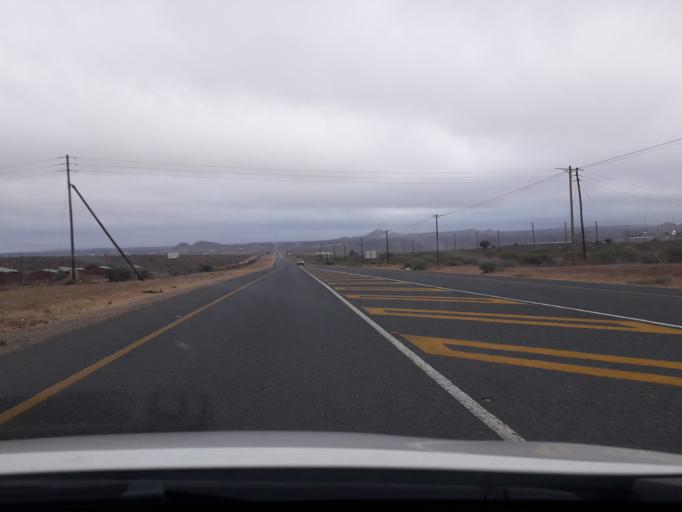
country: ZA
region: Limpopo
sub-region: Capricorn District Municipality
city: Dendron
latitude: -23.4739
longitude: 29.7306
